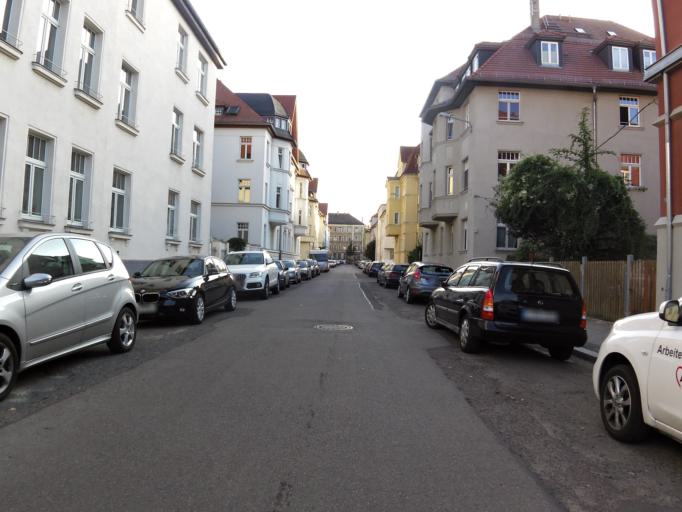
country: DE
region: Saxony
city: Leipzig
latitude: 51.3443
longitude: 12.3262
